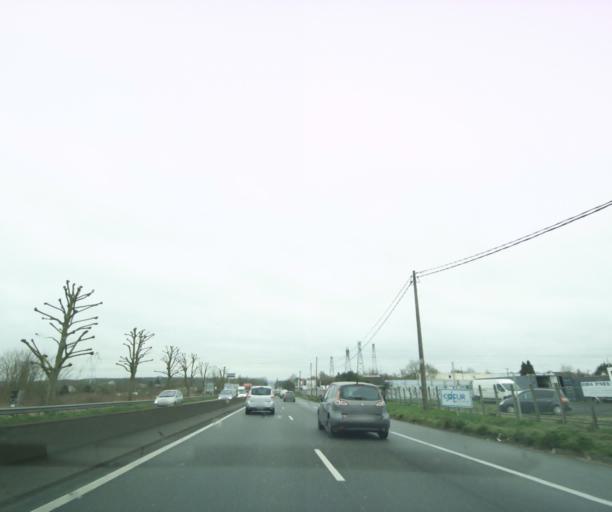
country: FR
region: Ile-de-France
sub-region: Departement de l'Essonne
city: Leuville-sur-Orge
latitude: 48.6135
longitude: 2.2546
